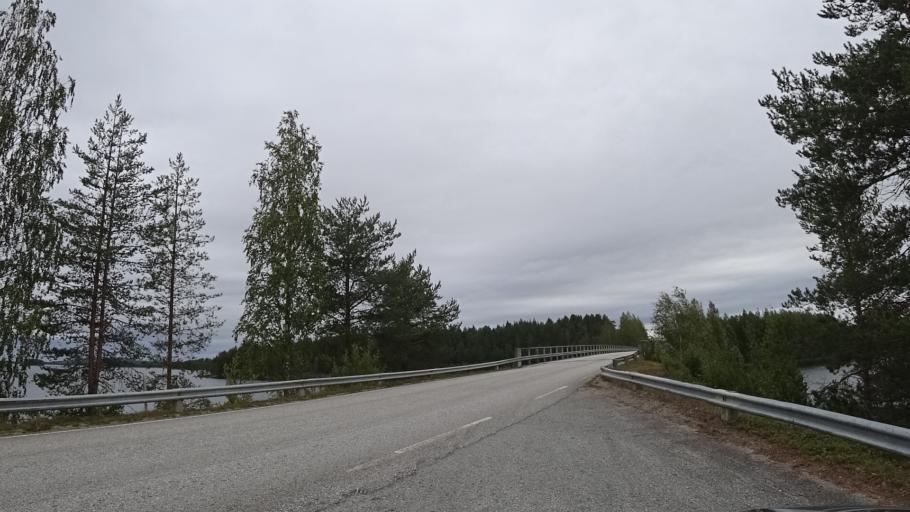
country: FI
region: North Karelia
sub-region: Pielisen Karjala
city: Lieksa
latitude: 63.3462
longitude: 30.2635
